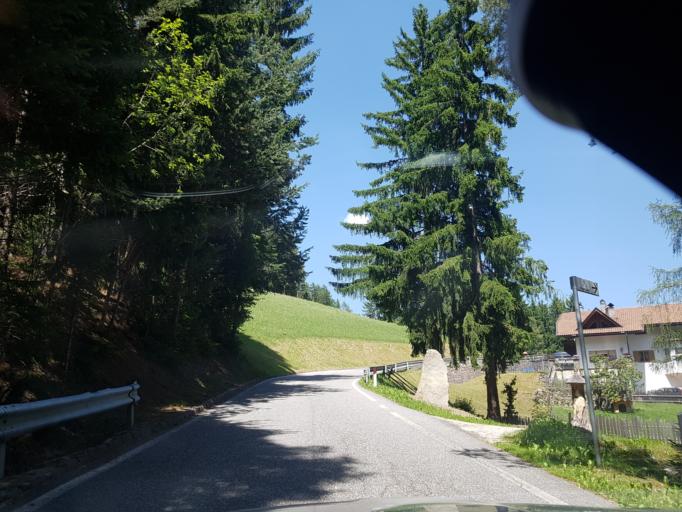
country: IT
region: Trentino-Alto Adige
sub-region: Bolzano
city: Villandro - Villanders
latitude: 46.6311
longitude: 11.5253
